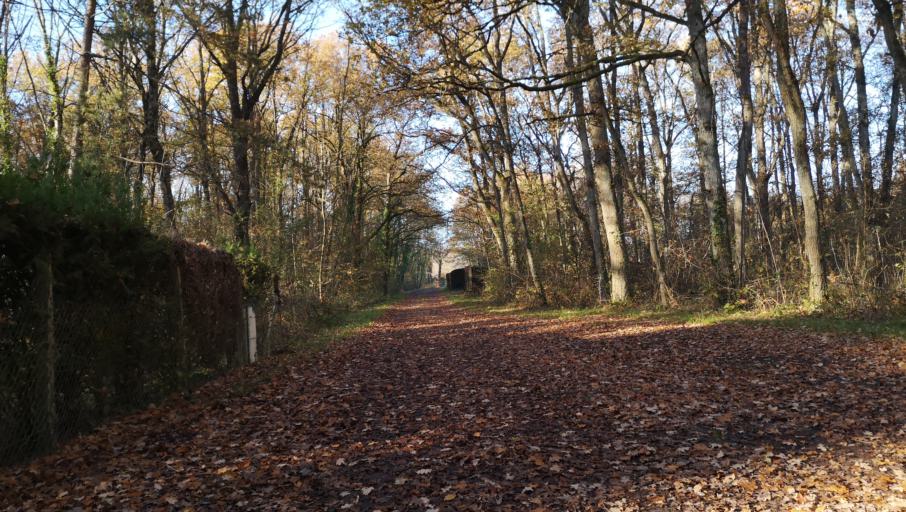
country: FR
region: Centre
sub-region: Departement du Loiret
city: Saran
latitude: 47.9367
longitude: 1.8547
